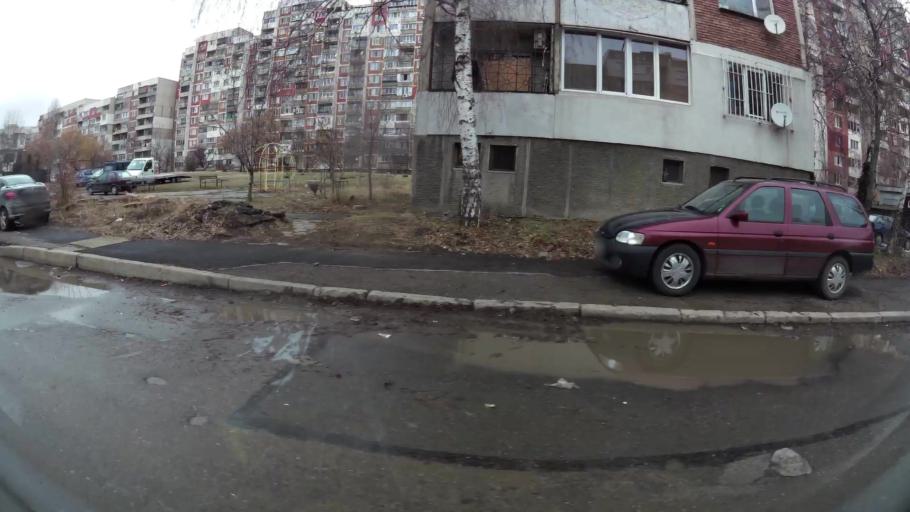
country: BG
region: Sofiya
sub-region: Obshtina Bozhurishte
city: Bozhurishte
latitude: 42.7307
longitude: 23.2505
